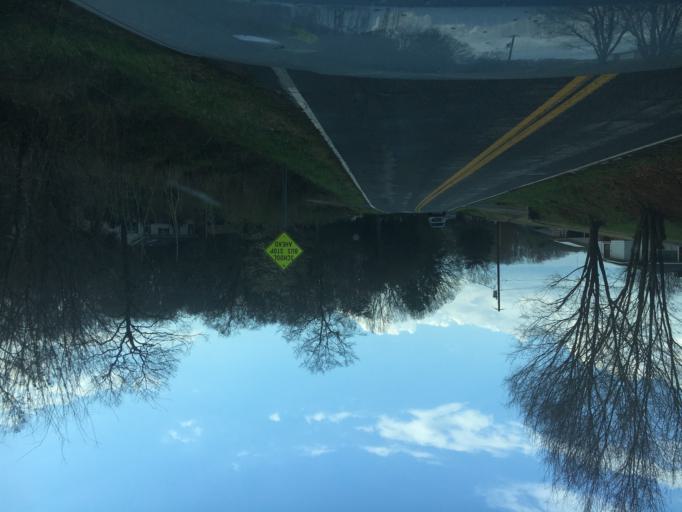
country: US
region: South Carolina
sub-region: Greenville County
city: Parker
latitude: 34.8522
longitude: -82.4955
